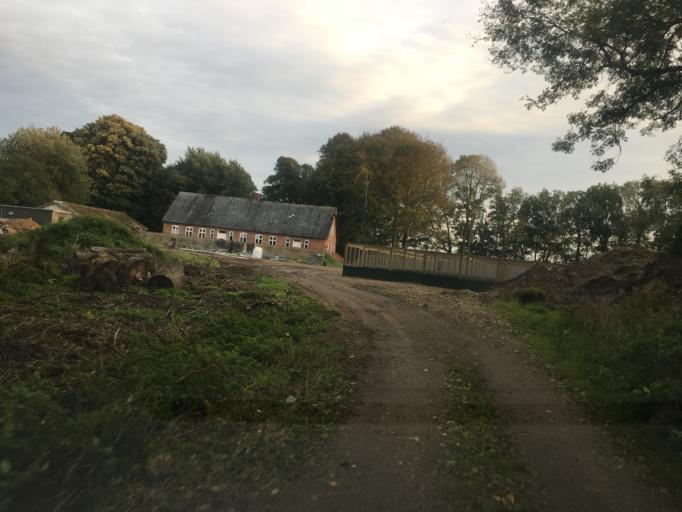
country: DK
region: South Denmark
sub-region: Tonder Kommune
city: Tonder
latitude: 54.9627
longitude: 8.8419
